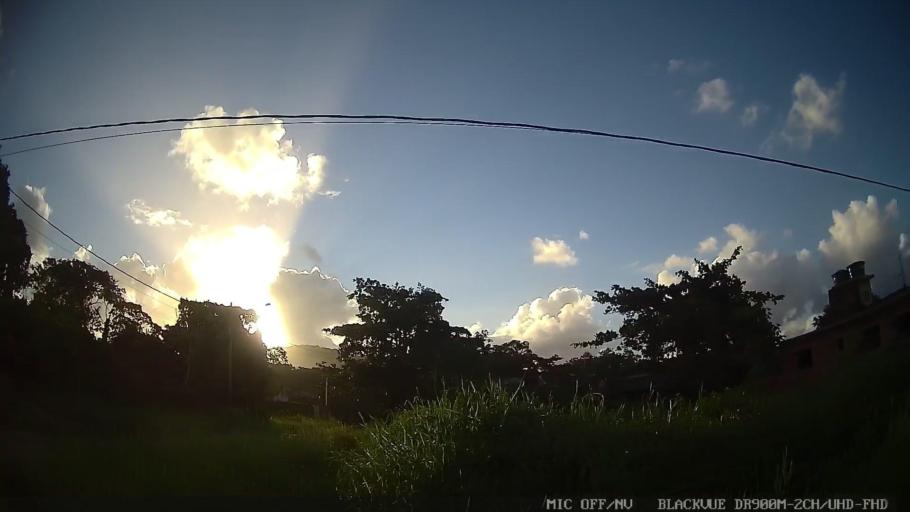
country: BR
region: Sao Paulo
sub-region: Itanhaem
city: Itanhaem
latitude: -24.1418
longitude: -46.7206
